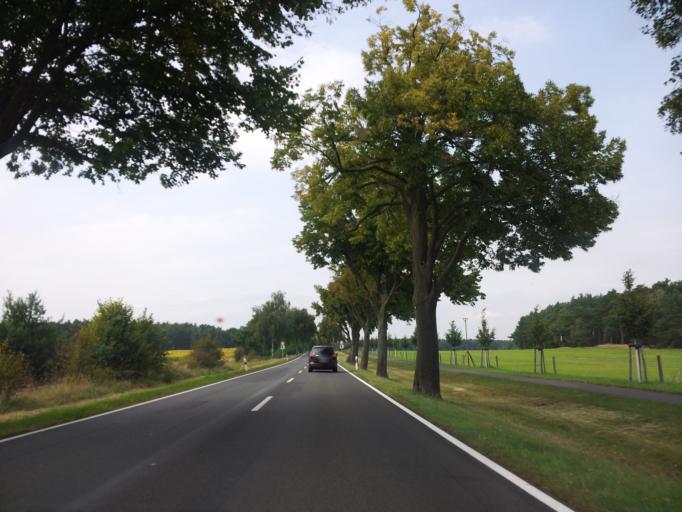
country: DE
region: Brandenburg
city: Belzig
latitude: 52.1184
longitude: 12.6428
